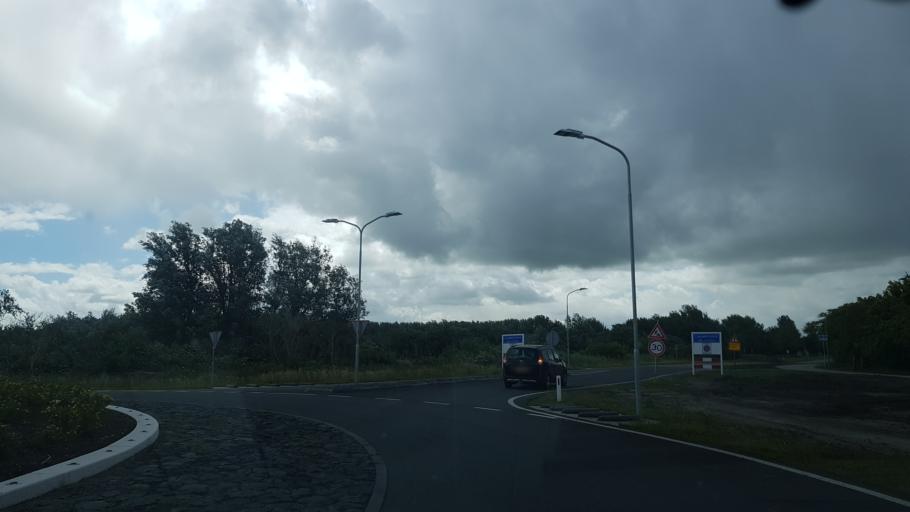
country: NL
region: Friesland
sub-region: Gemeente Dongeradeel
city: Anjum
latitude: 53.4075
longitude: 6.2111
